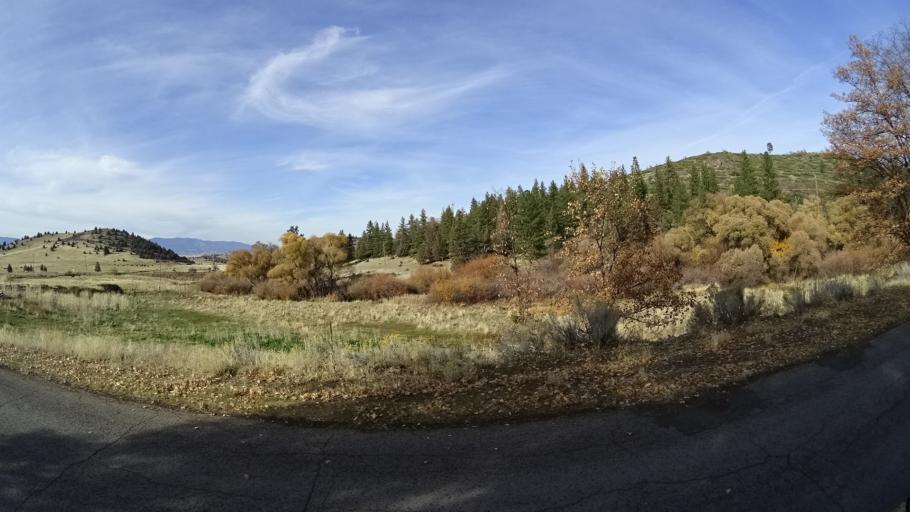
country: US
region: California
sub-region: Siskiyou County
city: Weed
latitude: 41.4671
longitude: -122.4117
